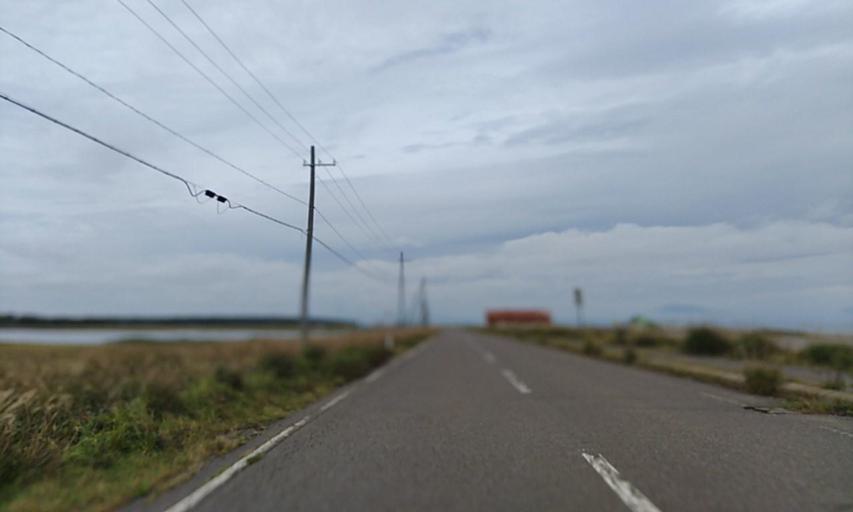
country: JP
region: Hokkaido
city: Shibetsu
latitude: 43.6023
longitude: 145.3048
